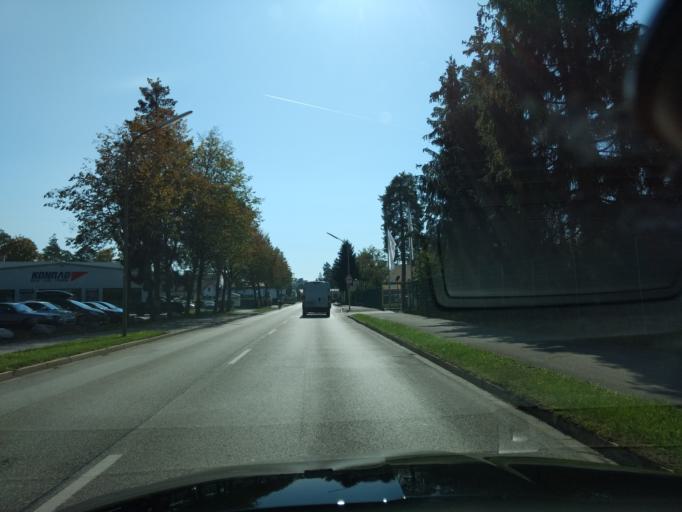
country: DE
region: Bavaria
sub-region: Upper Bavaria
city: Geretsried
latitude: 47.8822
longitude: 11.4664
